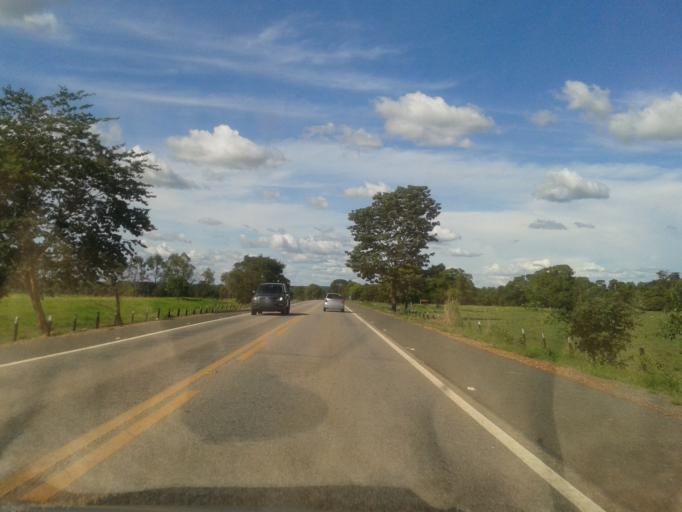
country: BR
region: Goias
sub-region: Mozarlandia
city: Mozarlandia
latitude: -15.0101
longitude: -50.5929
